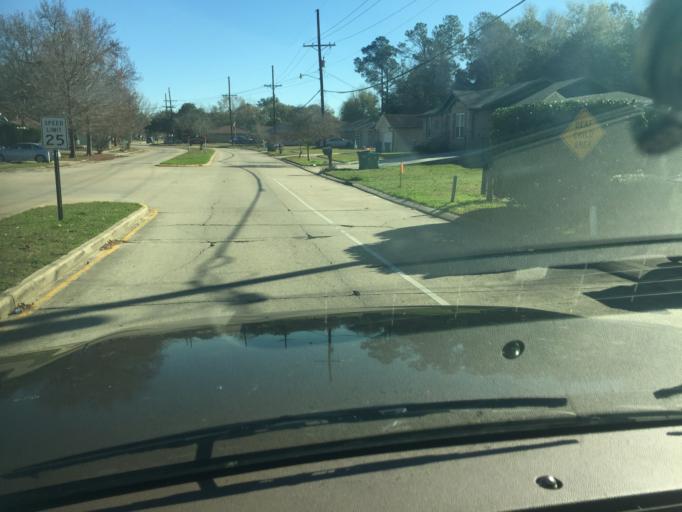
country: US
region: Louisiana
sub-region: Saint Tammany Parish
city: Slidell
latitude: 30.3014
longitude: -89.7730
